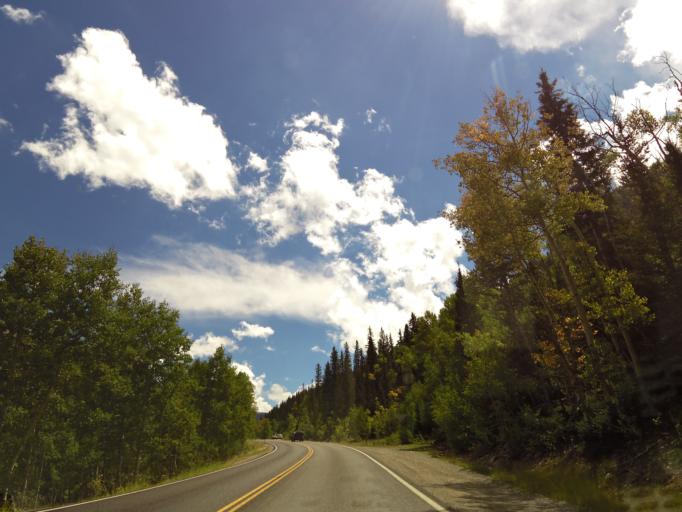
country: US
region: Colorado
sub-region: San Juan County
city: Silverton
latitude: 37.8043
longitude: -107.6788
